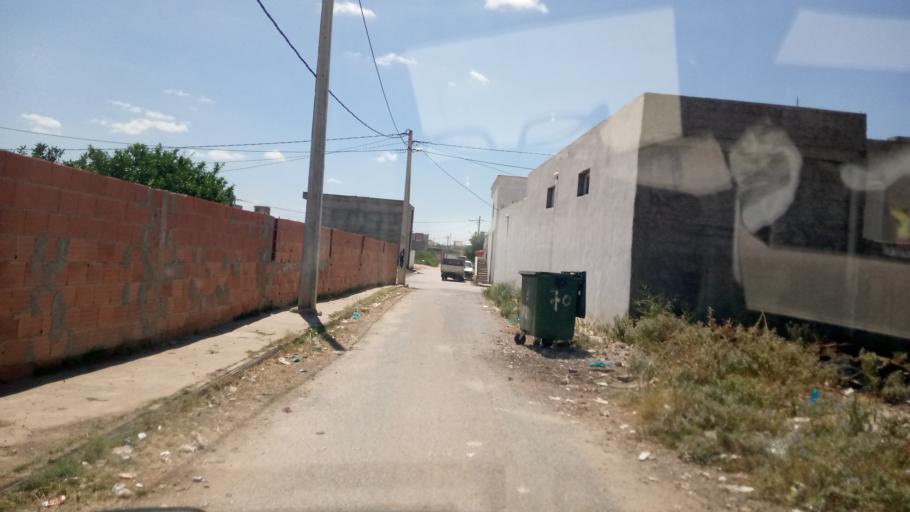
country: TN
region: Al Qayrawan
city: Sbikha
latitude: 36.1275
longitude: 10.0891
